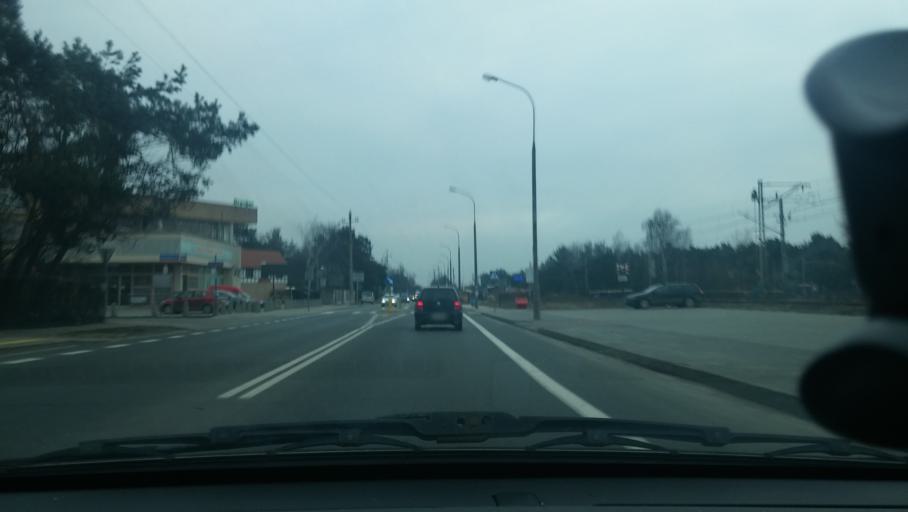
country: PL
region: Masovian Voivodeship
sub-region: Warszawa
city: Wawer
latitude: 52.1926
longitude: 21.1808
